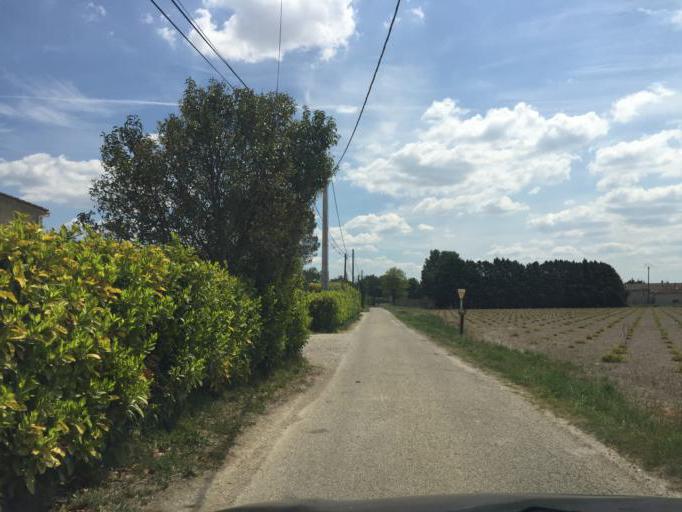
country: FR
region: Provence-Alpes-Cote d'Azur
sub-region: Departement du Vaucluse
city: Jonquieres
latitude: 44.1277
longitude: 4.8945
